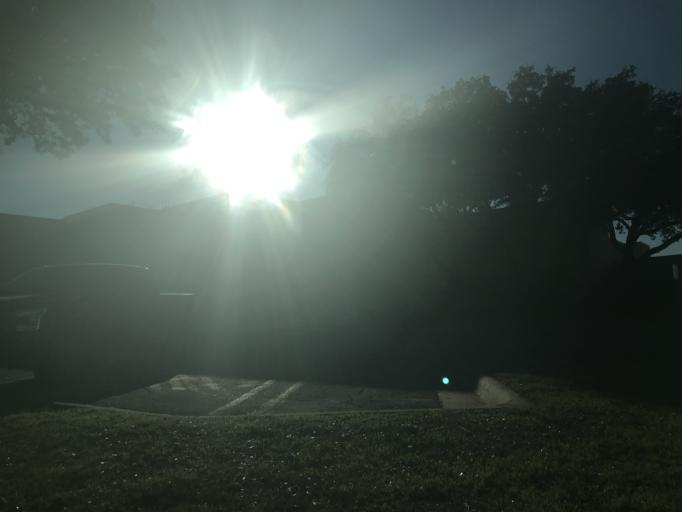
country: US
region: Texas
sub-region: Tom Green County
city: San Angelo
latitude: 31.4274
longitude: -100.4963
